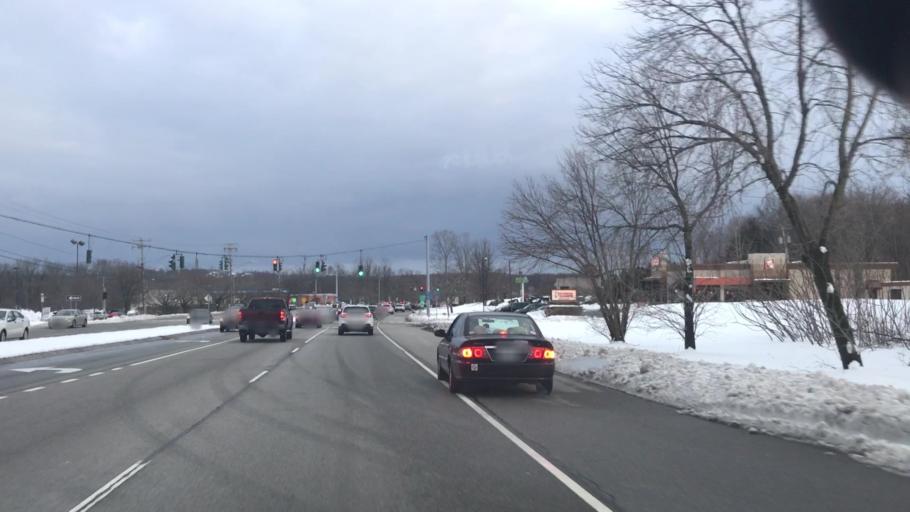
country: US
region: New York
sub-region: Dutchess County
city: Wappingers Falls
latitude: 41.5912
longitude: -73.9086
